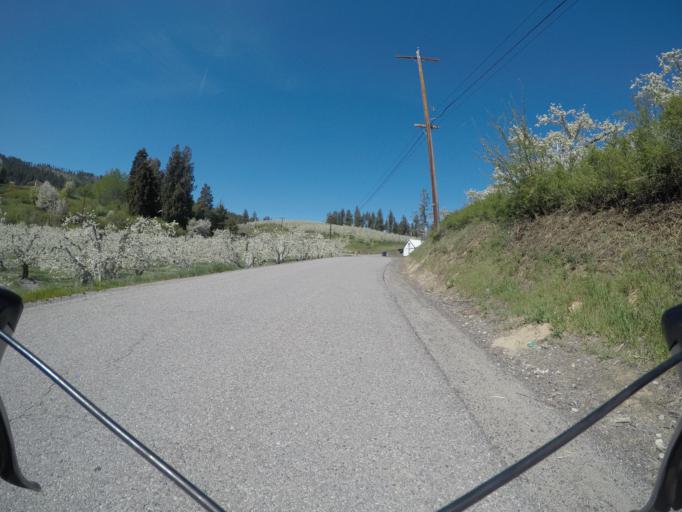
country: US
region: Washington
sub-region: Chelan County
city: Cashmere
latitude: 47.5394
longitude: -120.5708
